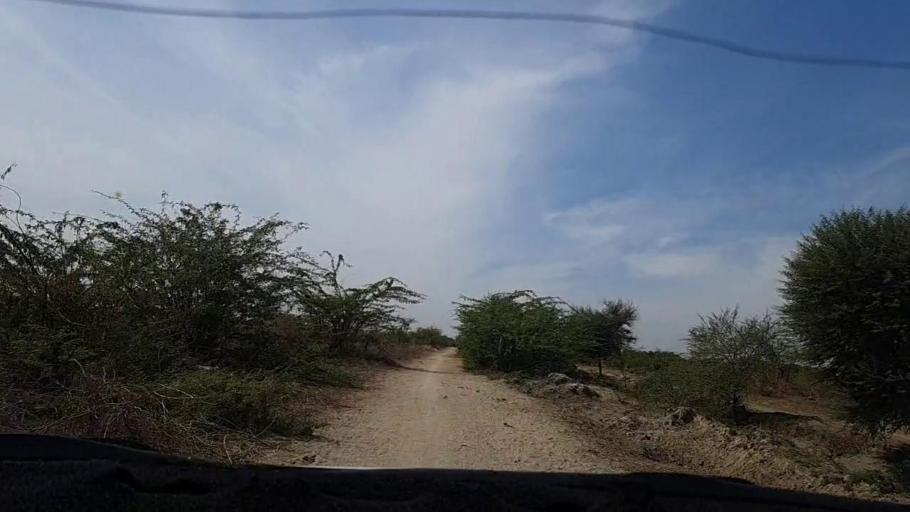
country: PK
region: Sindh
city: Dhoro Naro
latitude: 25.5165
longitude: 69.4795
